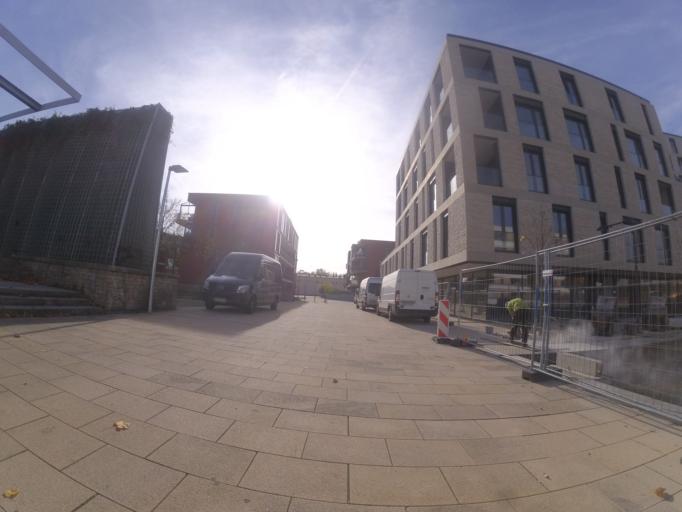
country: DE
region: Bavaria
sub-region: Swabia
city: Neu-Ulm
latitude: 48.3918
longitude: 10.0049
